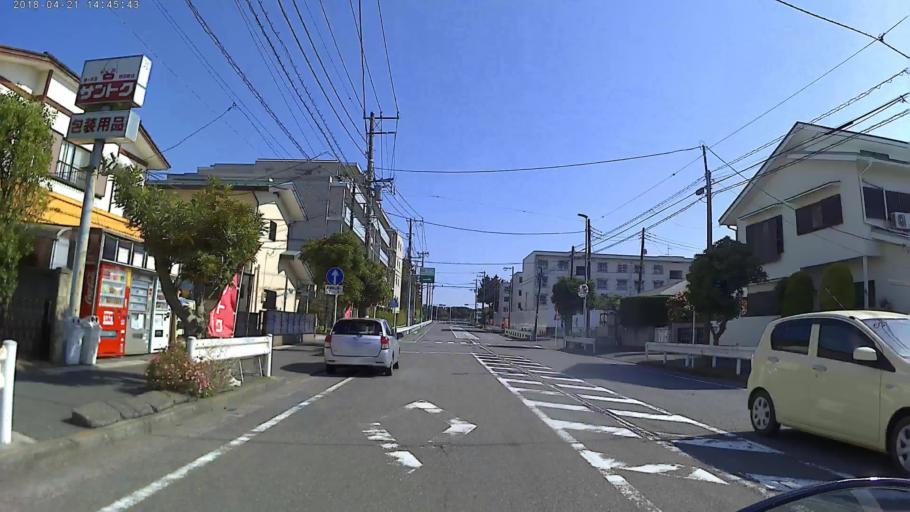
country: JP
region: Kanagawa
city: Hiratsuka
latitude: 35.3175
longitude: 139.3477
